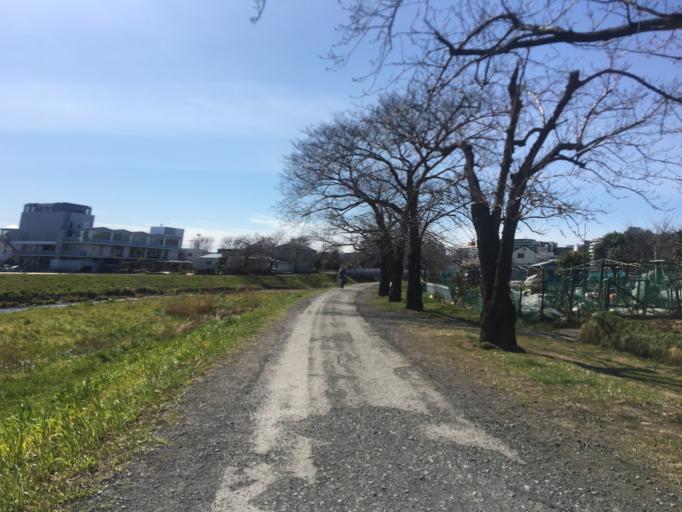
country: JP
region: Saitama
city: Asaka
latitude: 35.8095
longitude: 139.5887
